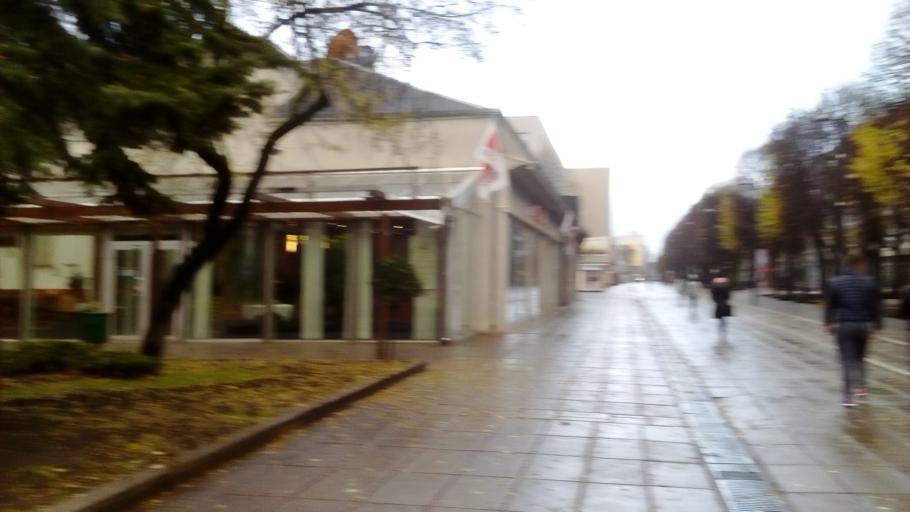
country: LT
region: Kauno apskritis
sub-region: Kaunas
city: Kaunas
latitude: 54.8972
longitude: 23.9052
